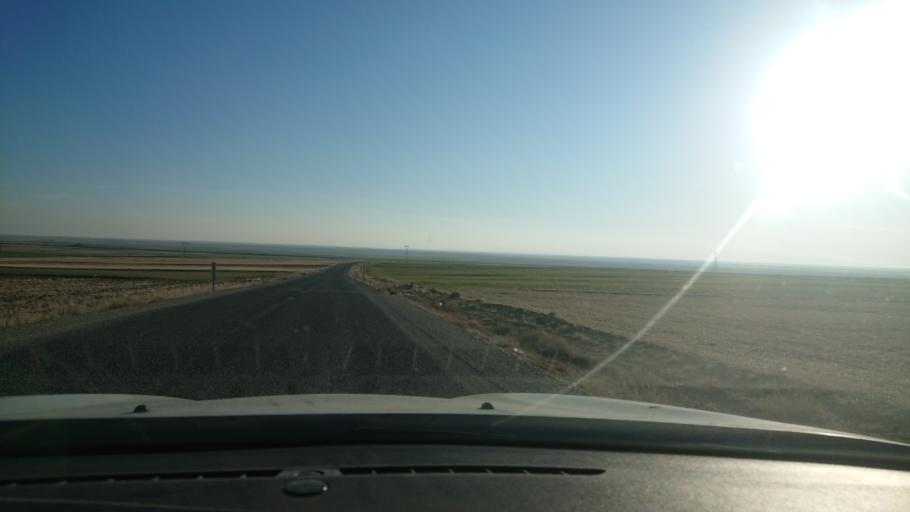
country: TR
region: Aksaray
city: Acipinar
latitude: 38.6780
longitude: 33.7326
